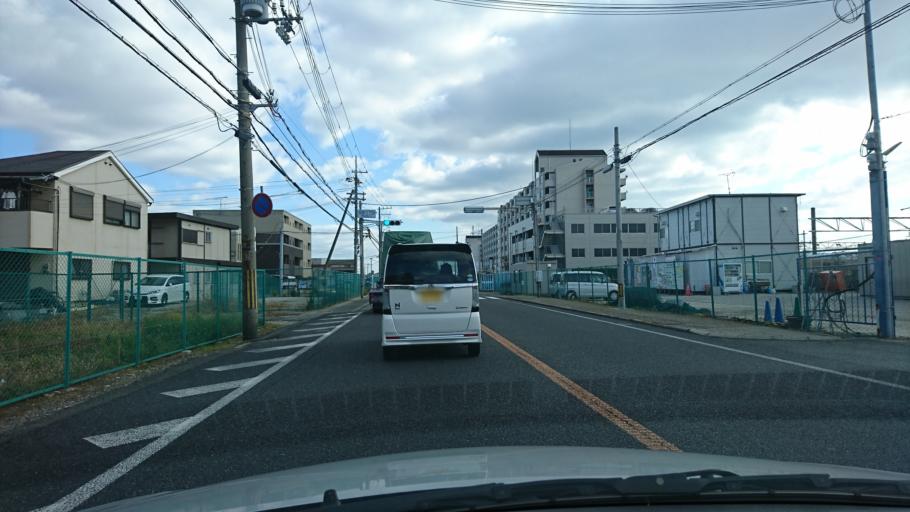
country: JP
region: Hyogo
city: Akashi
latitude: 34.6610
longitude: 134.9687
